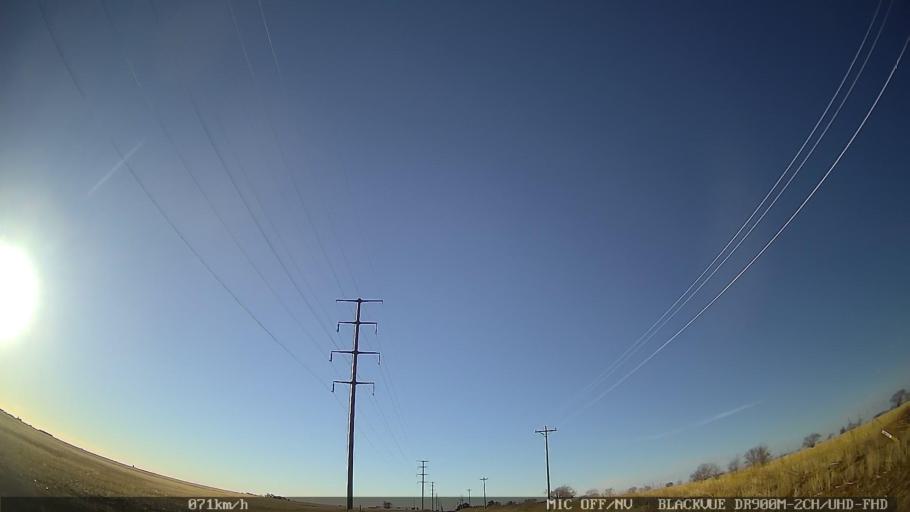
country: US
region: New Mexico
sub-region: Curry County
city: Clovis
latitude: 34.4292
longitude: -103.2494
